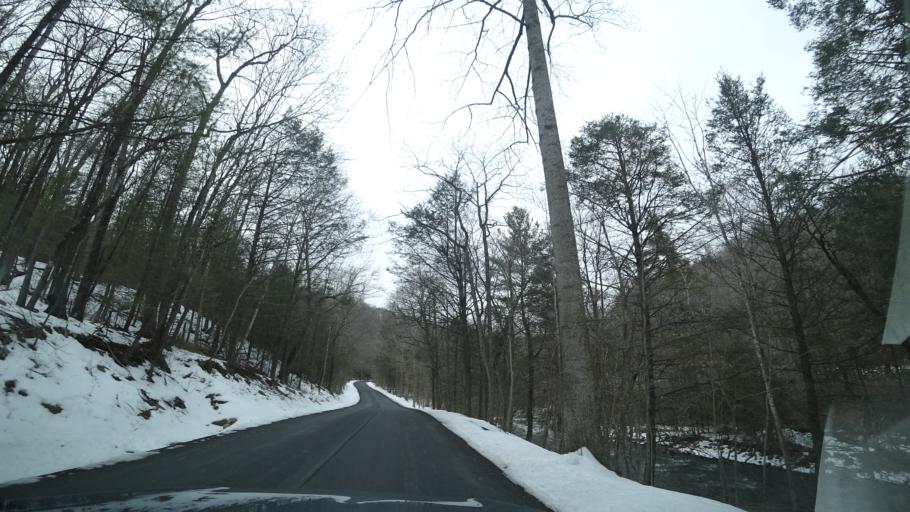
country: US
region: Virginia
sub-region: Shenandoah County
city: Woodstock
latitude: 39.0022
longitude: -78.6586
